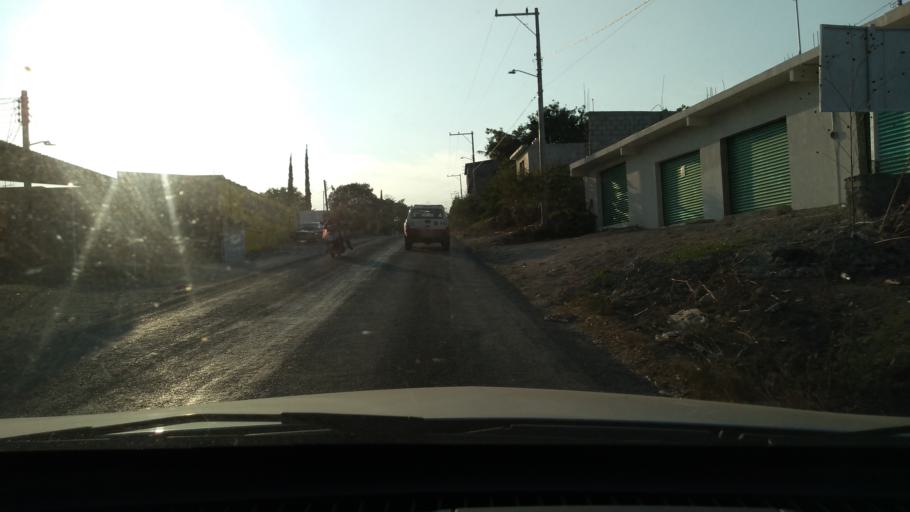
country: MX
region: Morelos
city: Puente de Ixtla
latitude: 18.6150
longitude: -99.3135
